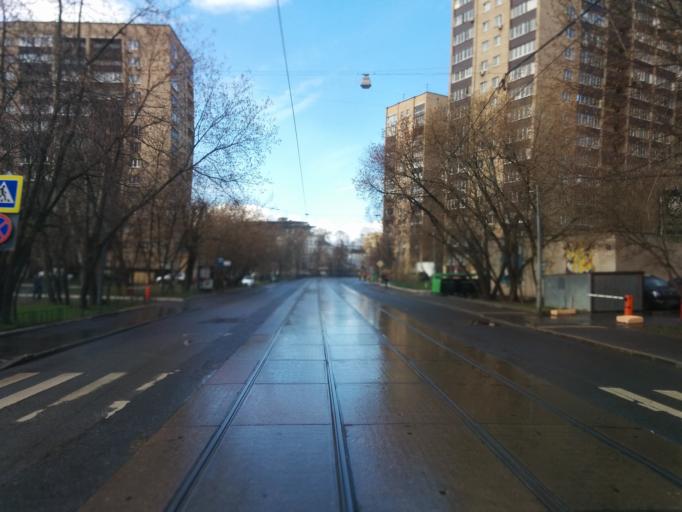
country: RU
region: Moscow
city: Mar'ina Roshcha
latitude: 55.7798
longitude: 37.6123
